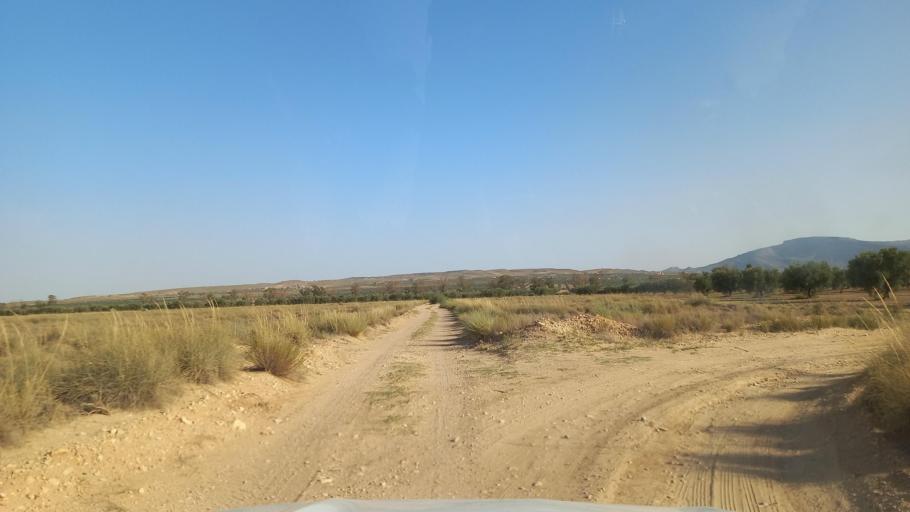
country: TN
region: Al Qasrayn
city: Kasserine
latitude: 35.2289
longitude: 8.9424
